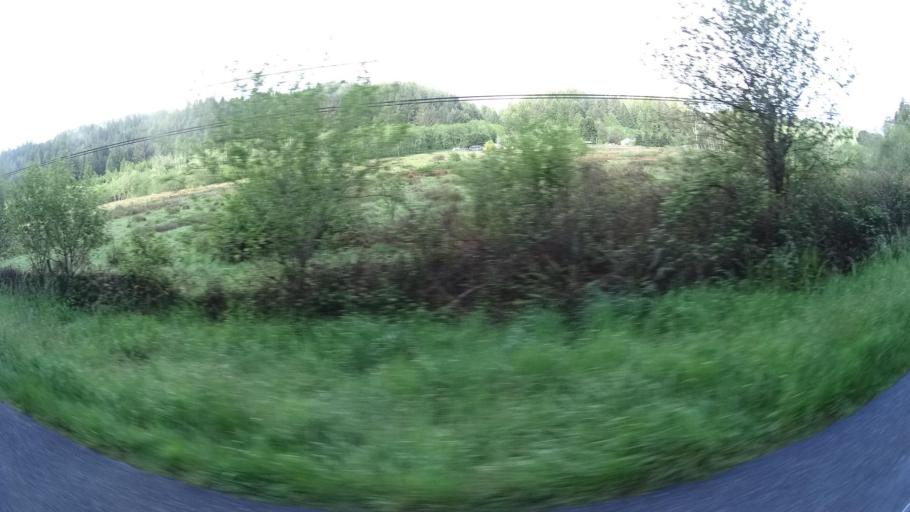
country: US
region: California
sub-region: Humboldt County
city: Blue Lake
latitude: 40.8846
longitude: -124.0304
